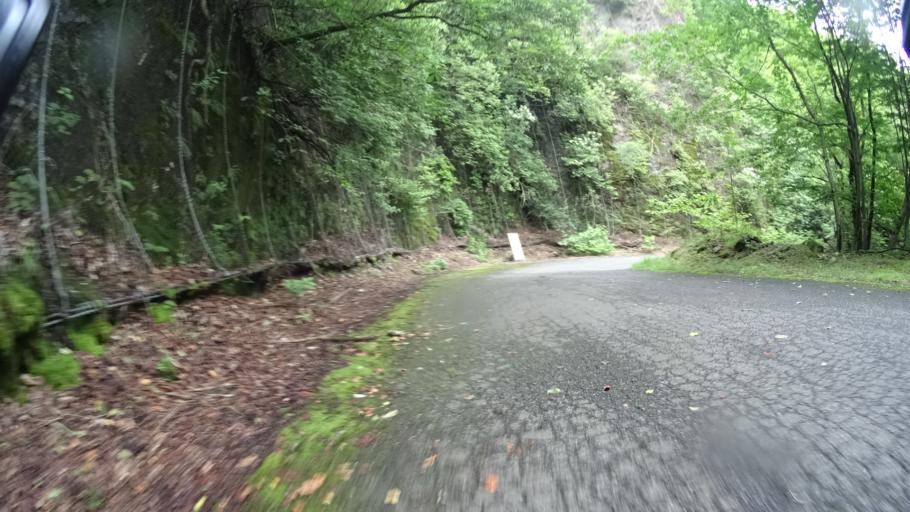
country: JP
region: Saitama
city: Chichibu
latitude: 35.8929
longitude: 139.1234
